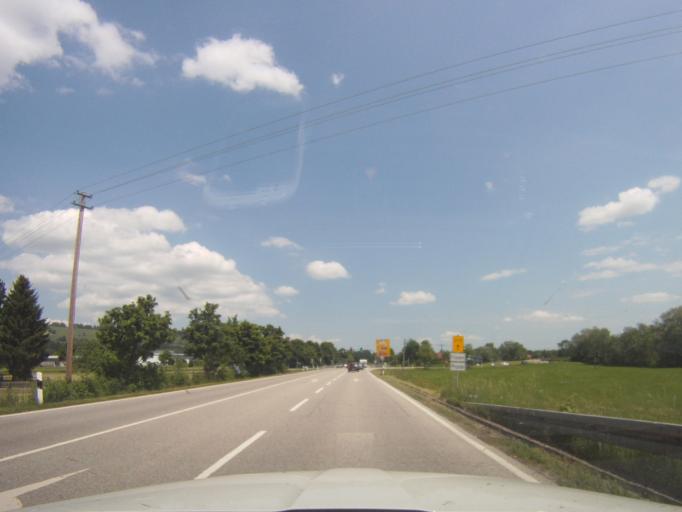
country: DE
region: Bavaria
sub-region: Swabia
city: Wertach
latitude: 47.6008
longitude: 10.4197
